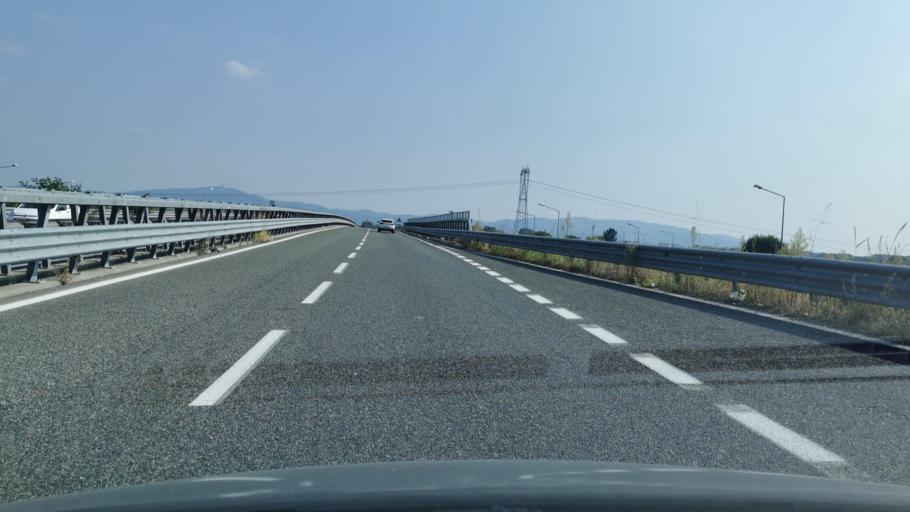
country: IT
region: Piedmont
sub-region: Provincia di Torino
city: Borgaro Torinese
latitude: 45.1323
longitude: 7.6552
